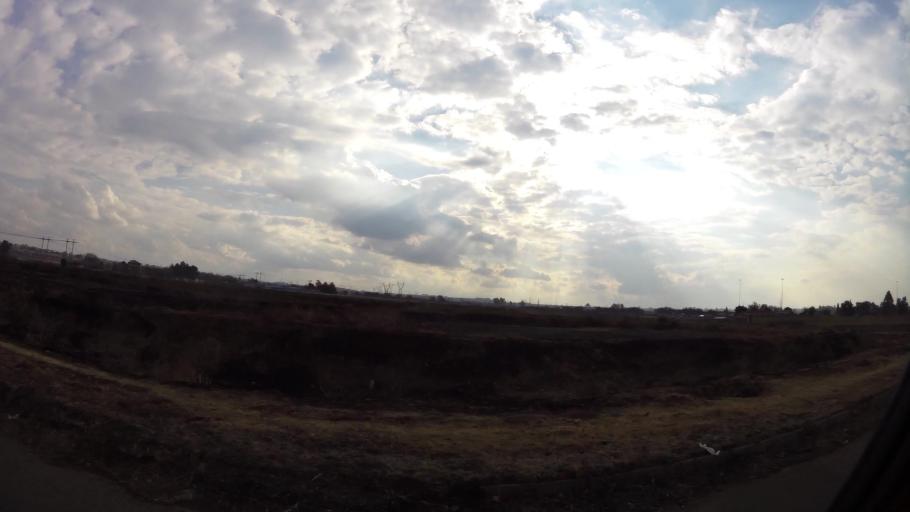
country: ZA
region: Gauteng
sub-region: Sedibeng District Municipality
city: Vereeniging
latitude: -26.6763
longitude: 27.8971
